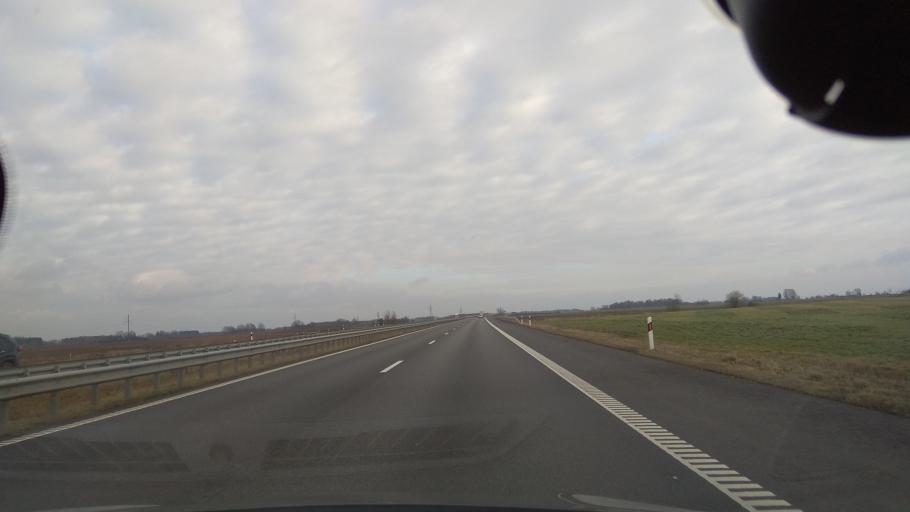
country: LT
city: Kazlu Ruda
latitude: 54.7001
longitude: 23.6125
